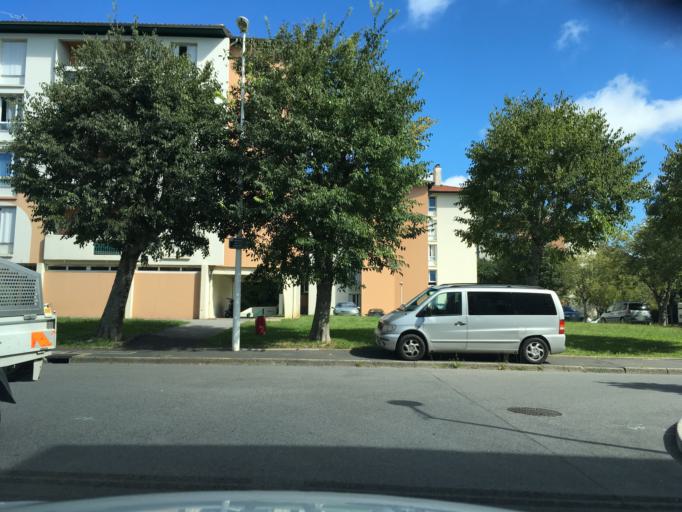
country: FR
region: Aquitaine
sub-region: Departement des Pyrenees-Atlantiques
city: Boucau
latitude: 43.5063
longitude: -1.4610
